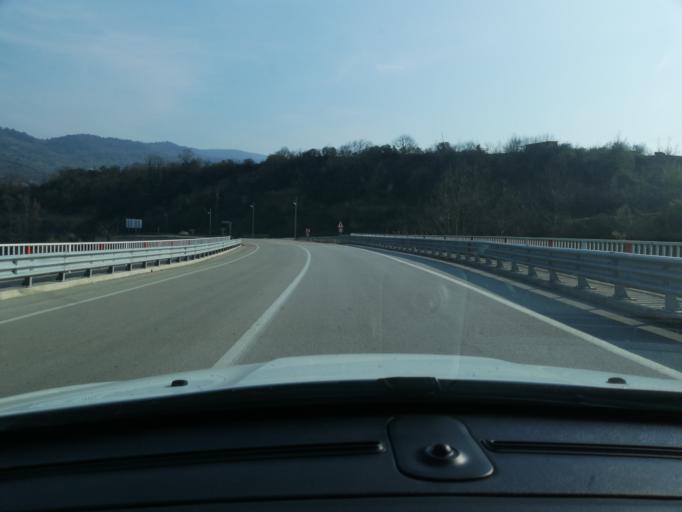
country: TR
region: Karabuk
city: Yenice
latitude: 41.2066
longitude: 32.3660
